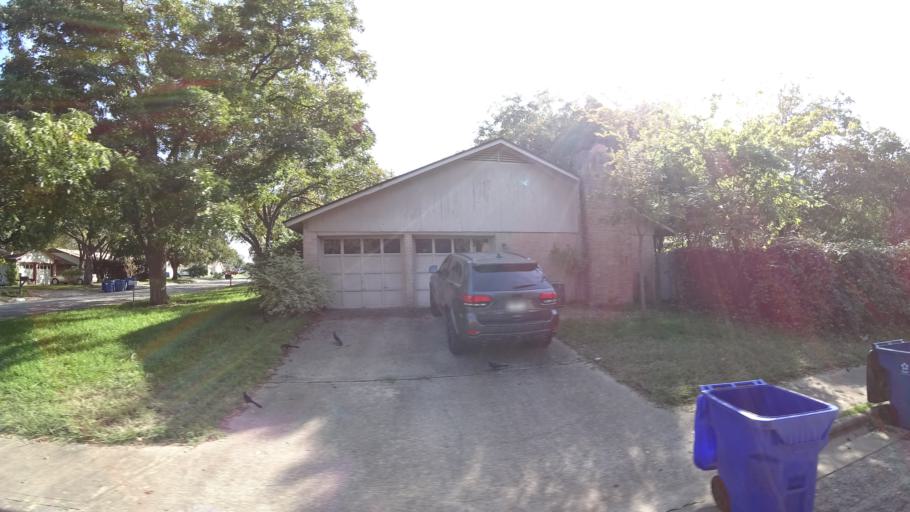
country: US
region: Texas
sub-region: Williamson County
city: Anderson Mill
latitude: 30.4518
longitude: -97.7994
